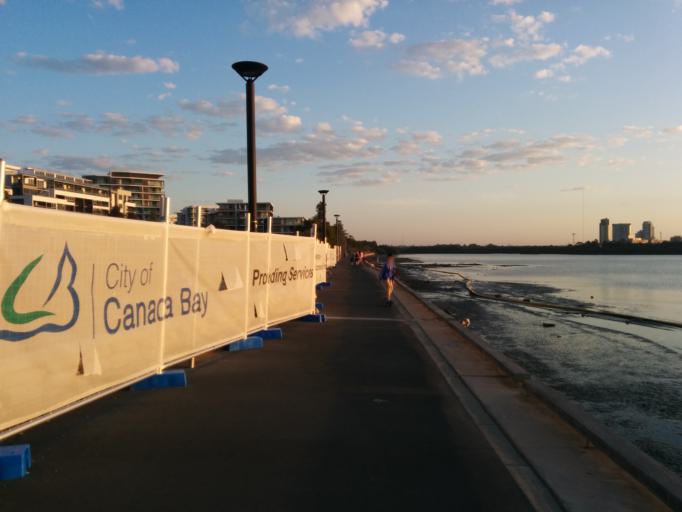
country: AU
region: New South Wales
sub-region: Canada Bay
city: Rhodes
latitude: -33.8288
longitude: 151.0832
